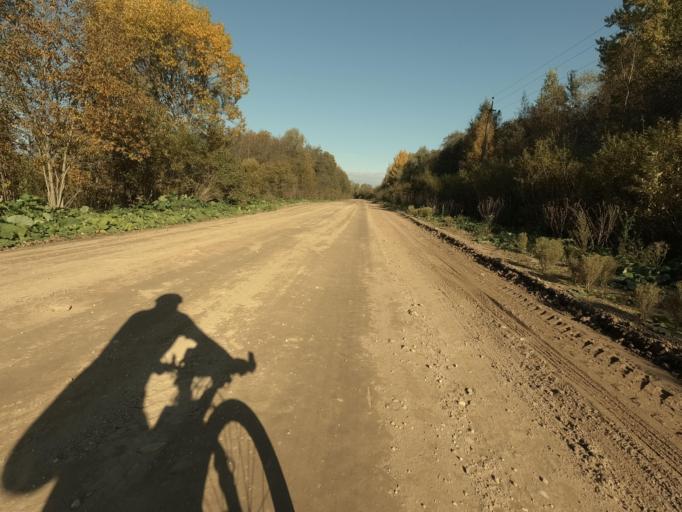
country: RU
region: Novgorod
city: Batetskiy
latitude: 58.8773
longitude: 30.7263
